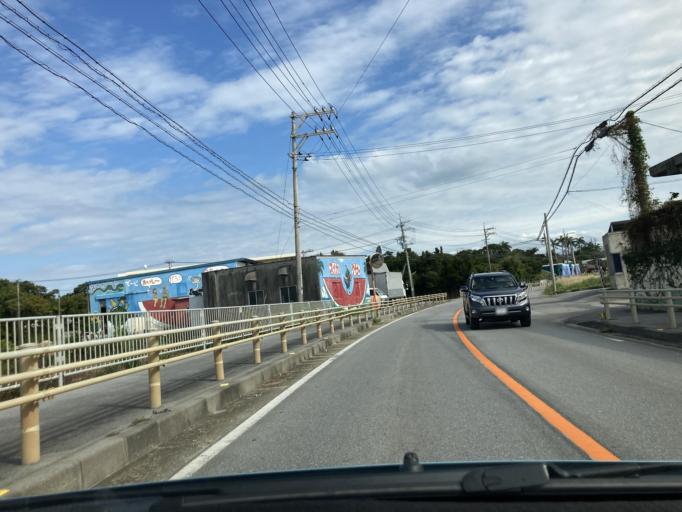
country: JP
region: Okinawa
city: Nago
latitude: 26.6957
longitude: 127.9521
